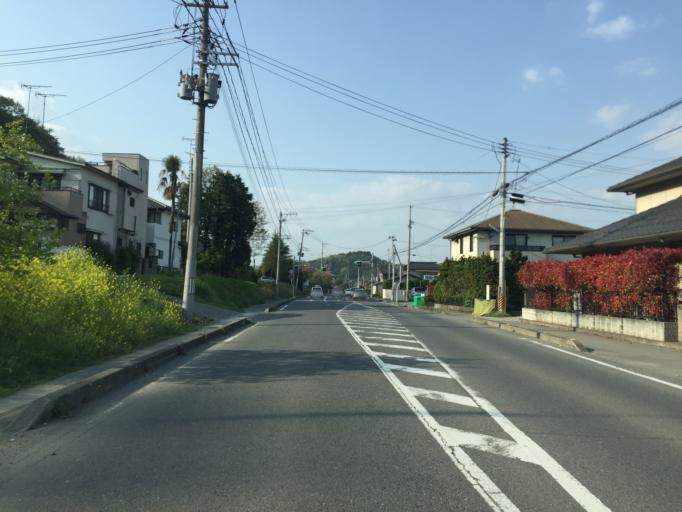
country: JP
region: Fukushima
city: Iwaki
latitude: 36.9932
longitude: 140.8539
